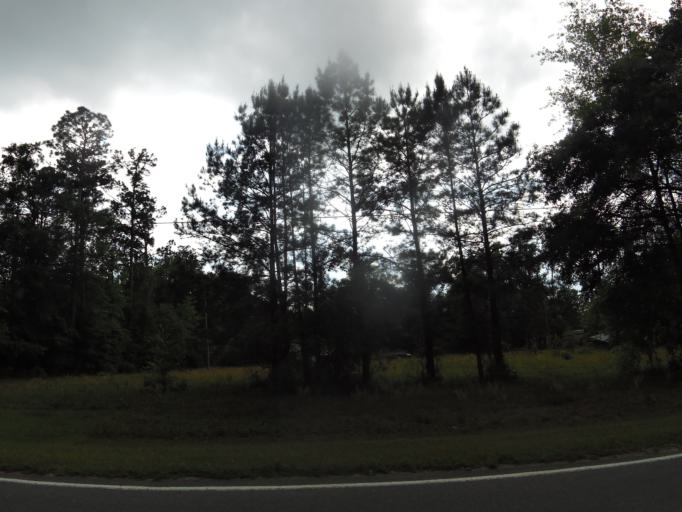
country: US
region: Georgia
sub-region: Charlton County
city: Folkston
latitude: 30.8395
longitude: -81.9935
